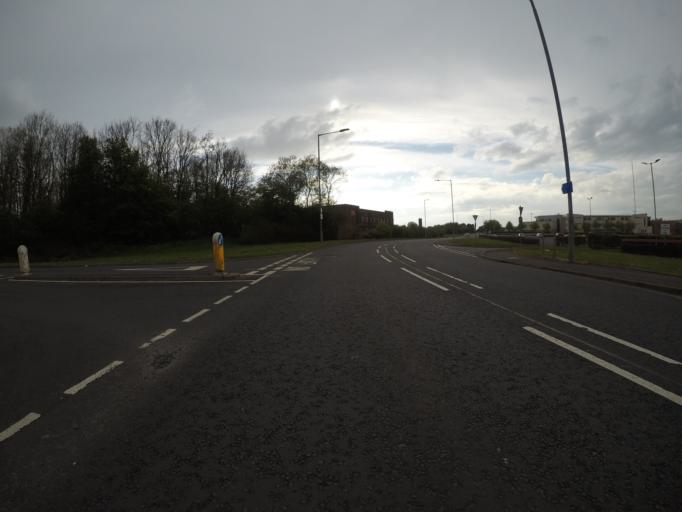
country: GB
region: Scotland
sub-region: North Ayrshire
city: Dreghorn
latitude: 55.6066
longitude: -4.6302
